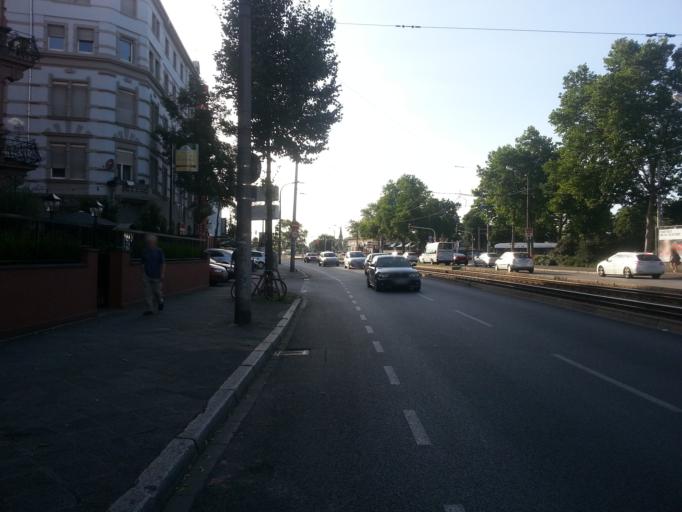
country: DE
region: Baden-Wuerttemberg
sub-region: Karlsruhe Region
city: Mannheim
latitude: 49.4919
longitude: 8.4738
